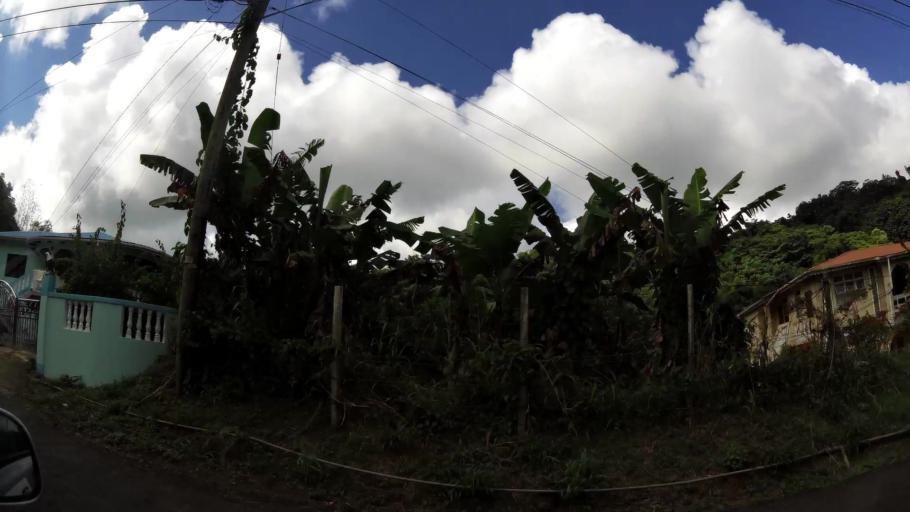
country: GD
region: Saint Andrew
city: Grenville
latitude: 12.1295
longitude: -61.6597
